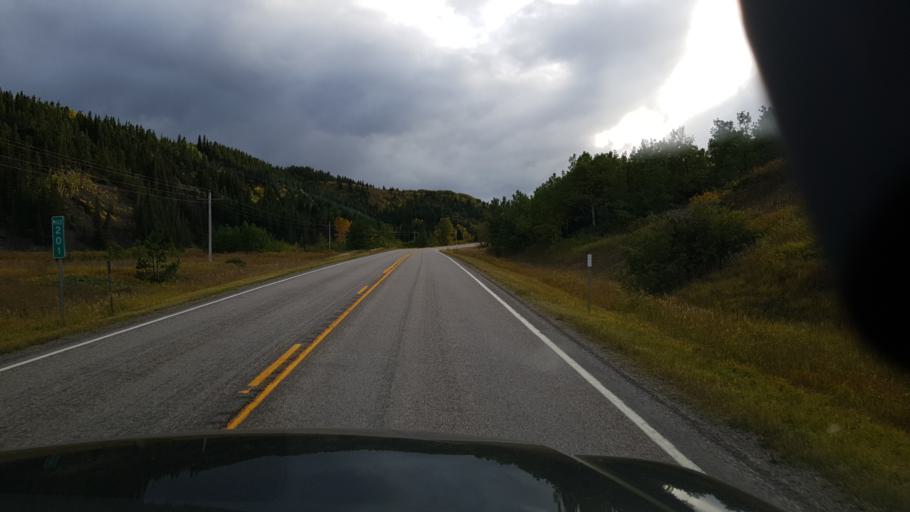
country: US
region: Montana
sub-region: Glacier County
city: South Browning
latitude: 48.3505
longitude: -113.3054
